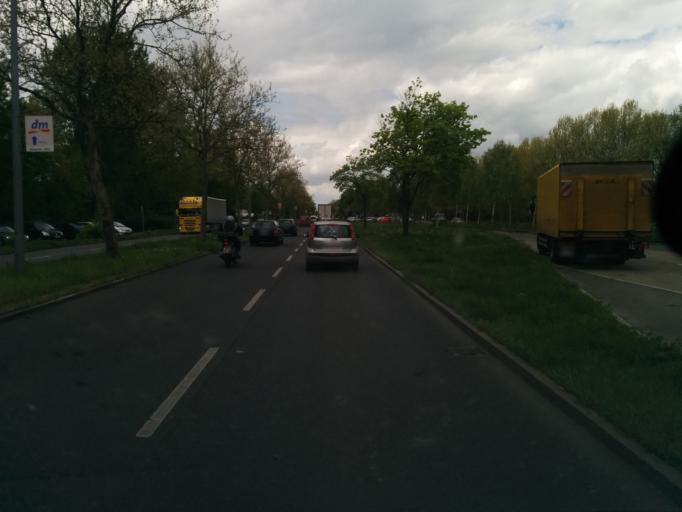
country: DE
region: Berlin
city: Staaken
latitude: 52.5225
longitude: 13.1512
